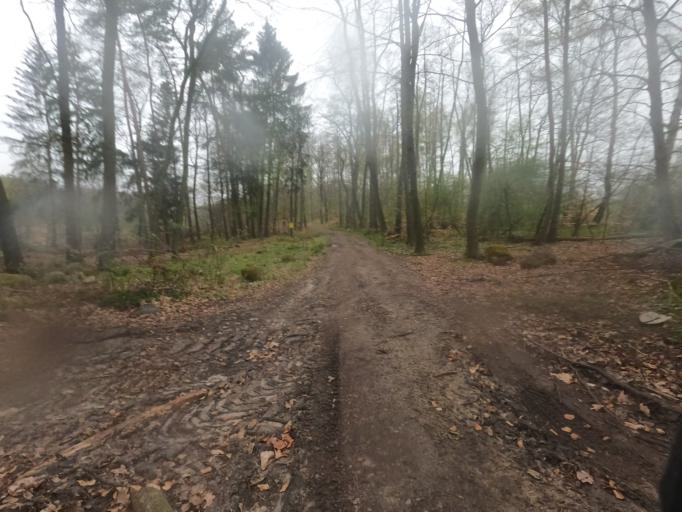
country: PL
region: West Pomeranian Voivodeship
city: Trzcinsko Zdroj
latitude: 52.9267
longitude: 14.7136
